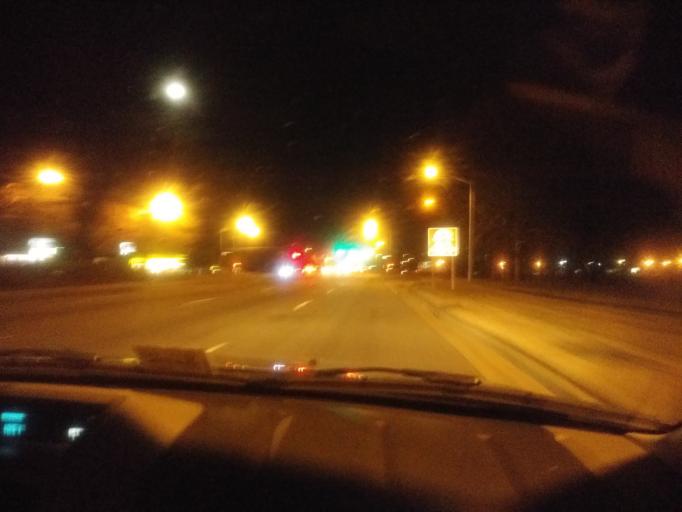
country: US
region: Virginia
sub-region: City of Chesapeake
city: Chesapeake
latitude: 36.8052
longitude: -76.1912
